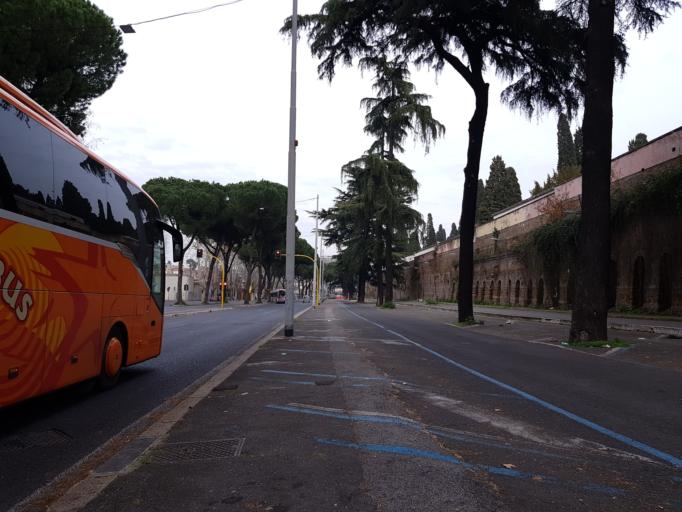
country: IT
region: Latium
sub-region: Citta metropolitana di Roma Capitale
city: Rome
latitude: 41.9047
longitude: 12.5213
